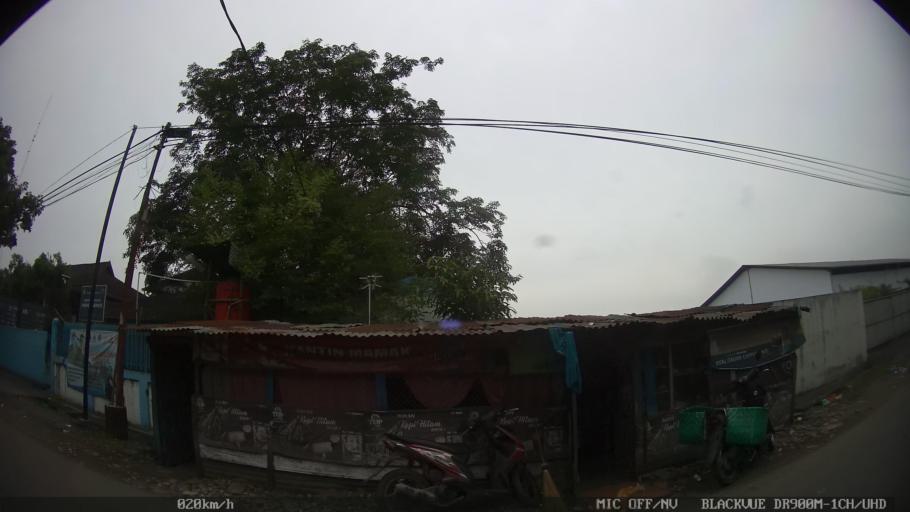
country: ID
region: North Sumatra
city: Deli Tua
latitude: 3.5382
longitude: 98.7270
